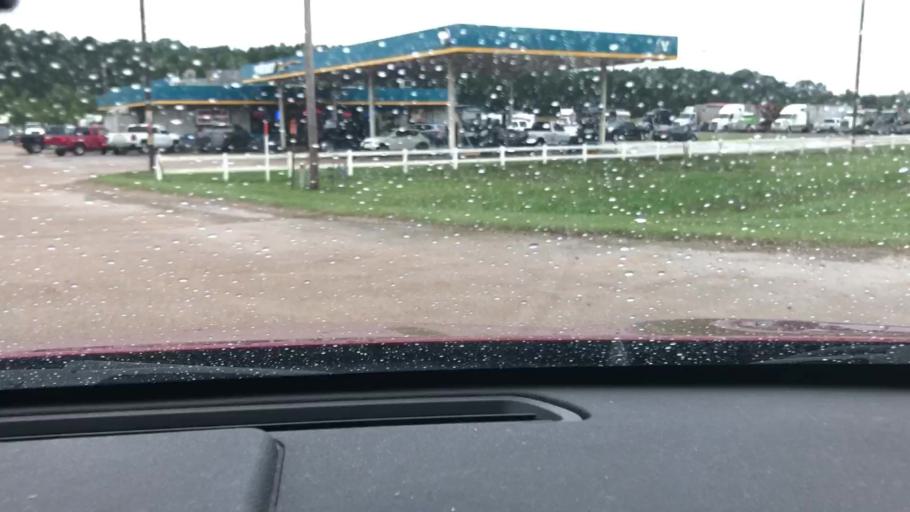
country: US
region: Arkansas
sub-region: Columbia County
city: Magnolia
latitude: 33.2960
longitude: -93.2516
